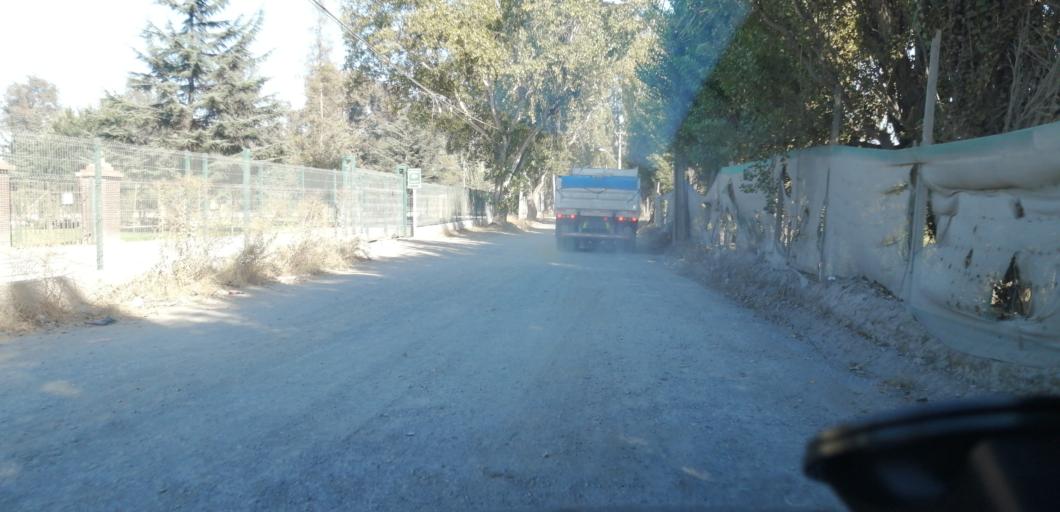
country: CL
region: Santiago Metropolitan
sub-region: Provincia de Santiago
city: Lo Prado
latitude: -33.4632
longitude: -70.7701
